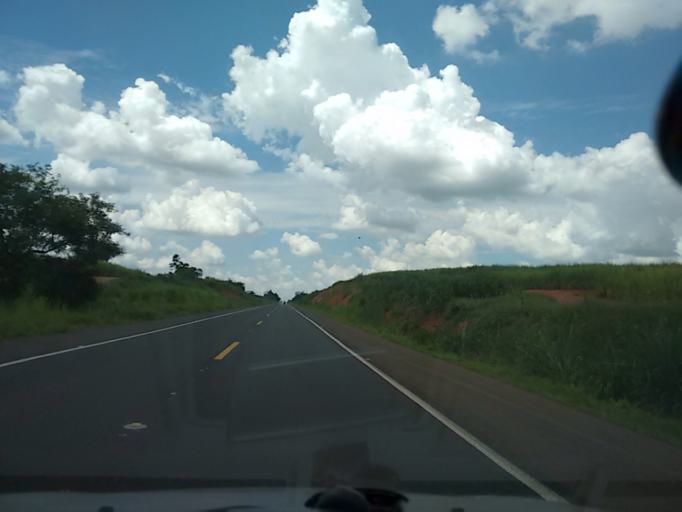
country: BR
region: Sao Paulo
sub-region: Osvaldo Cruz
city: Osvaldo Cruz
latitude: -21.8589
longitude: -50.8444
